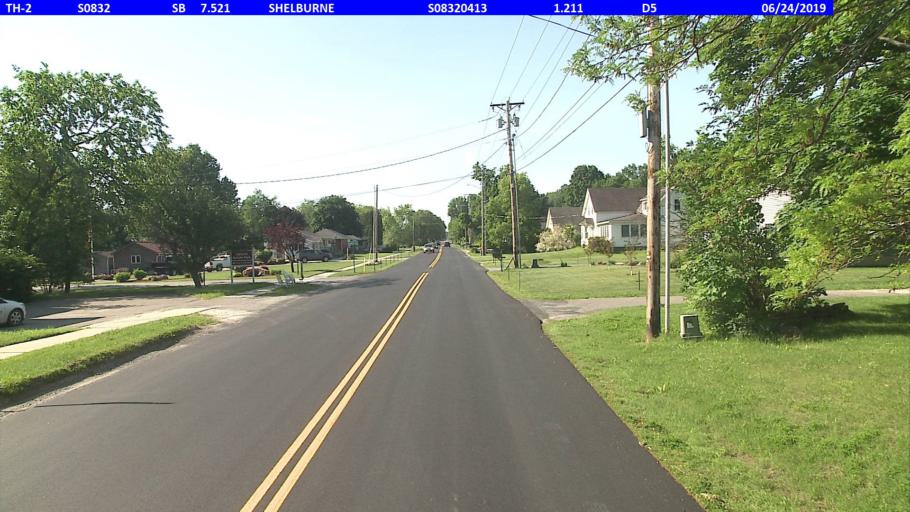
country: US
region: Vermont
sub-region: Chittenden County
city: Burlington
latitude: 44.3723
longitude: -73.2252
